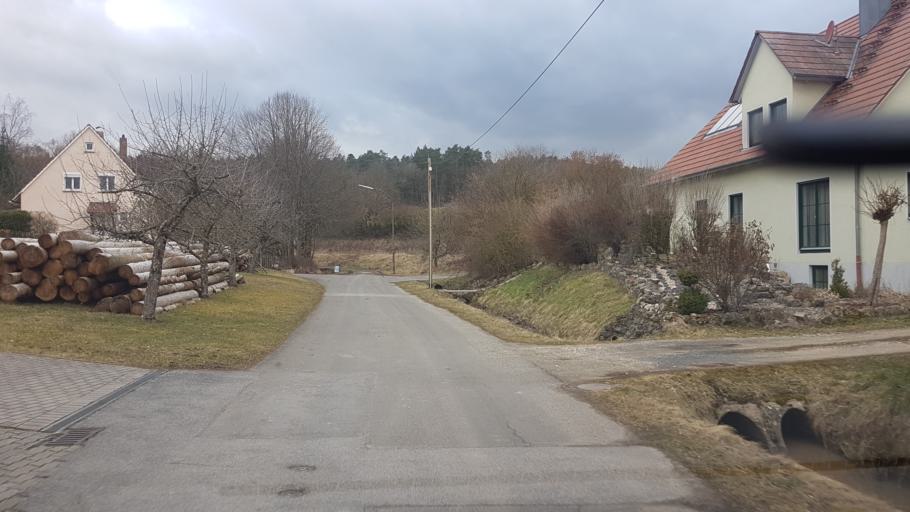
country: DE
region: Bavaria
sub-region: Upper Franconia
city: Reckendorf
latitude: 49.9990
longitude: 10.8091
